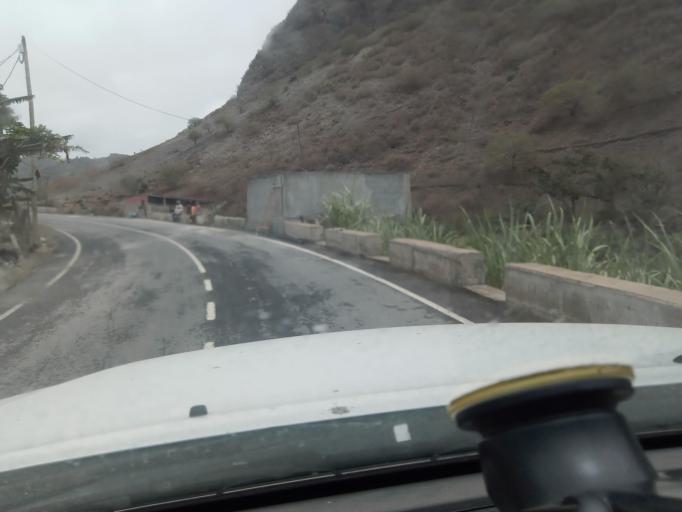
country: CV
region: Sao Miguel
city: Calheta
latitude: 15.1465
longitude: -23.6131
